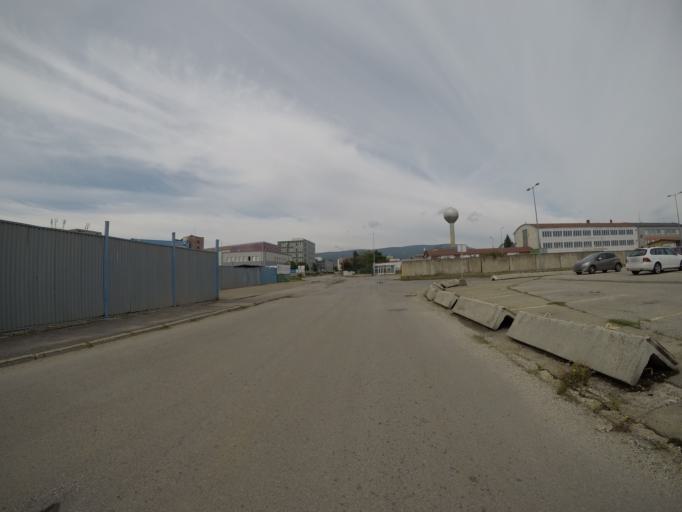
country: SK
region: Trenciansky
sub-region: Okres Nove Mesto nad Vahom
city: Nove Mesto nad Vahom
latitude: 48.7486
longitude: 17.8400
